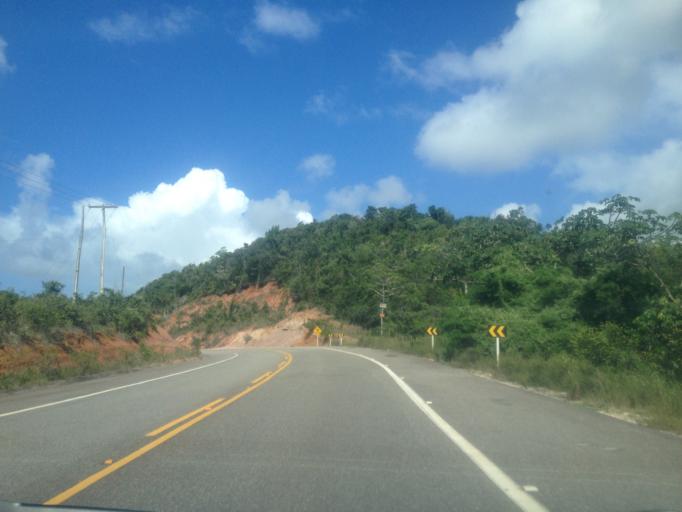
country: BR
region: Sergipe
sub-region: Indiaroba
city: Indiaroba
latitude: -11.4856
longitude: -37.4831
